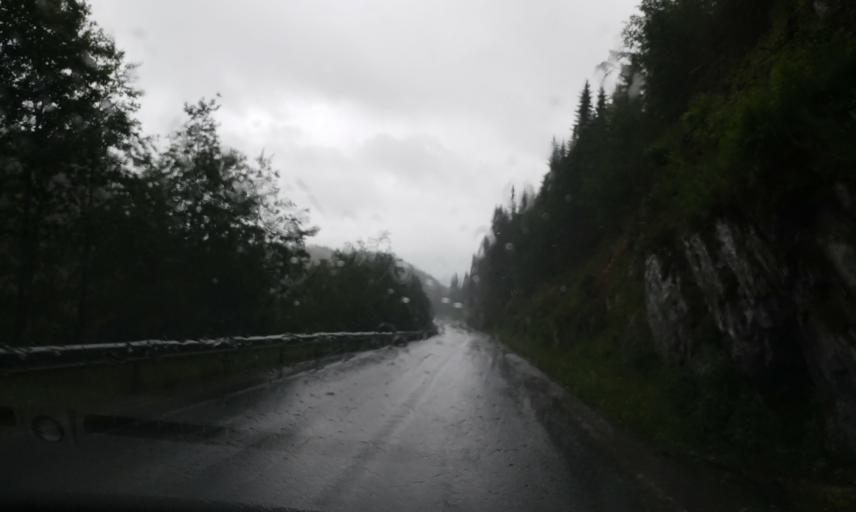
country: NO
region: Sor-Trondelag
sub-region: Selbu
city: Mebonden
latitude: 63.3190
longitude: 11.0841
